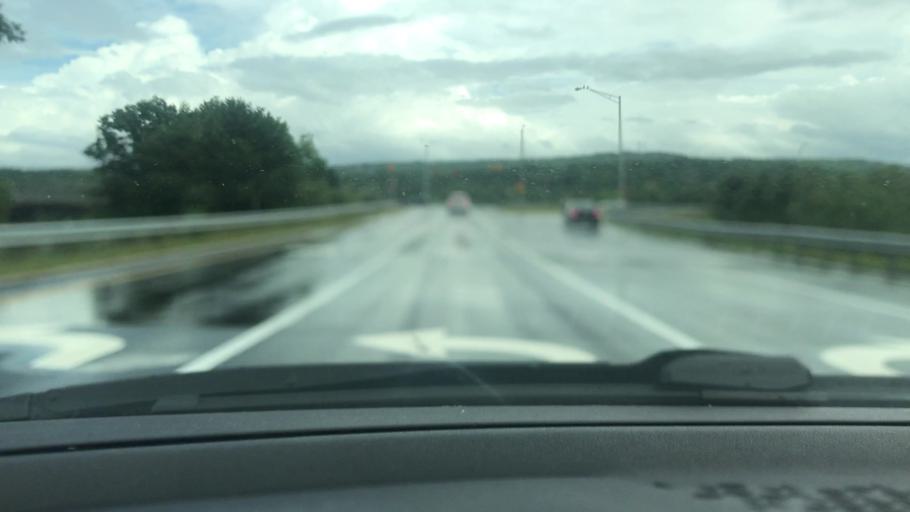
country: US
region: New Hampshire
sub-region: Merrimack County
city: East Concord
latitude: 43.2348
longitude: -71.4722
